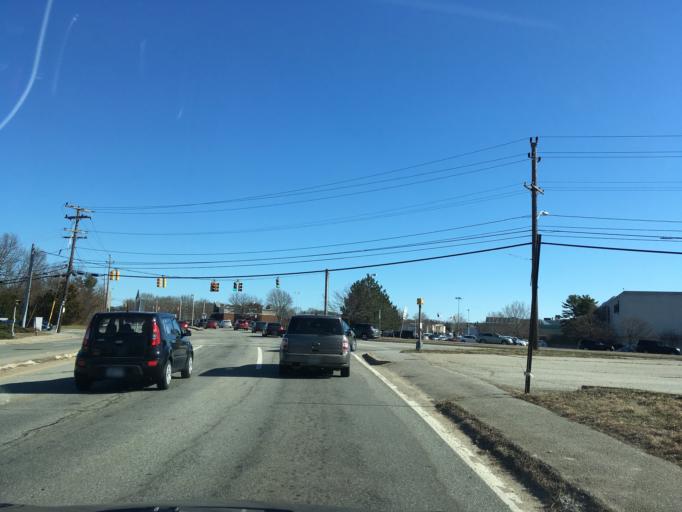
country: US
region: Rhode Island
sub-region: Kent County
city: West Warwick
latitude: 41.7280
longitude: -71.4764
